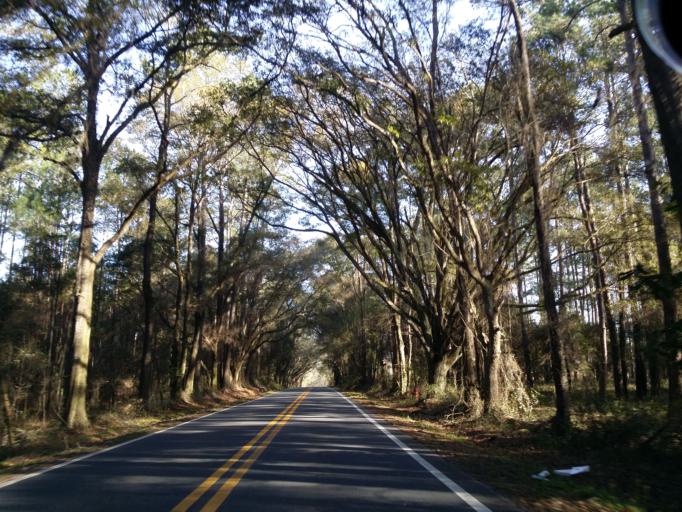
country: US
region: Florida
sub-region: Leon County
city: Woodville
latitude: 30.3818
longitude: -84.1553
